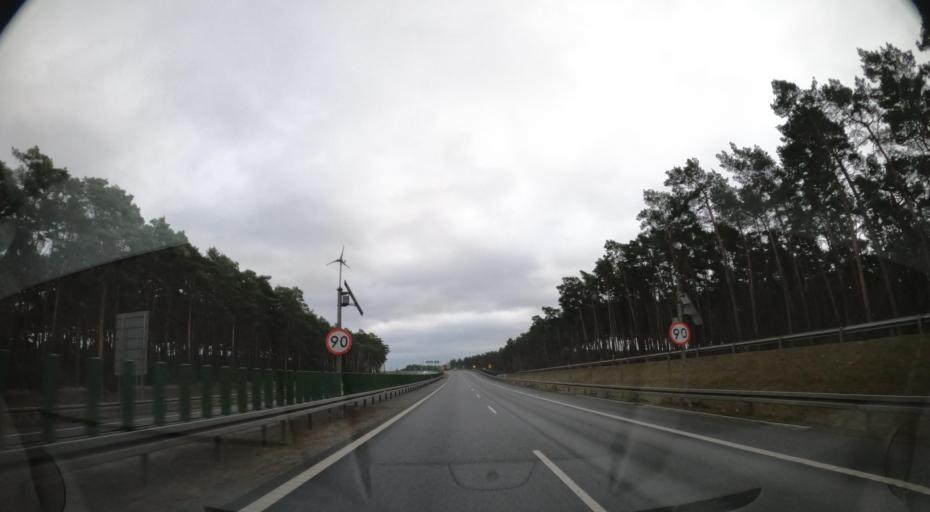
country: PL
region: Kujawsko-Pomorskie
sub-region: Bydgoszcz
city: Bydgoszcz
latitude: 53.0540
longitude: 17.9837
